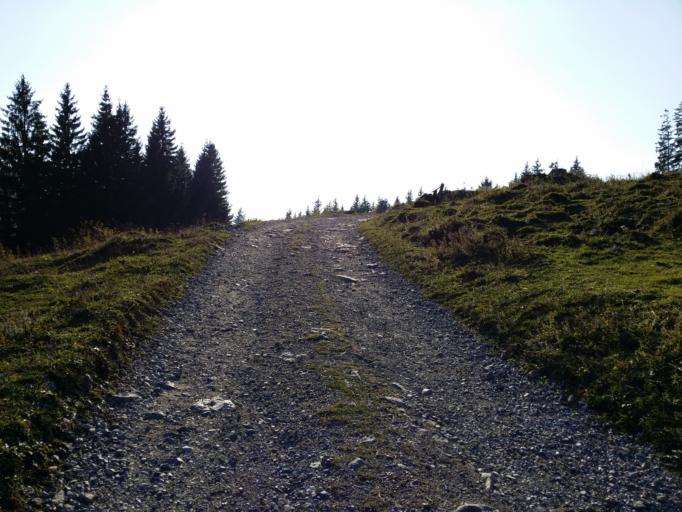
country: AT
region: Tyrol
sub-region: Politischer Bezirk Kufstein
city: Erl
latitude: 47.7239
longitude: 12.2292
